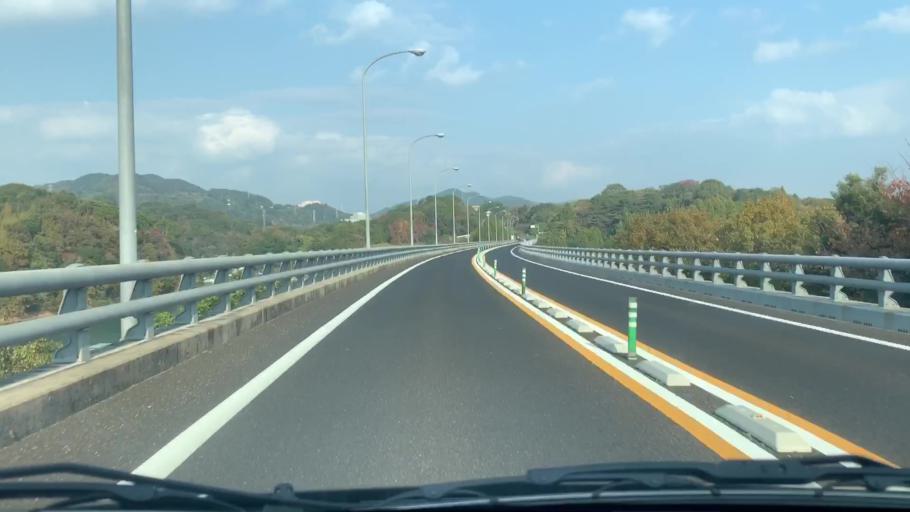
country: JP
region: Nagasaki
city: Sasebo
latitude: 33.0770
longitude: 129.7698
